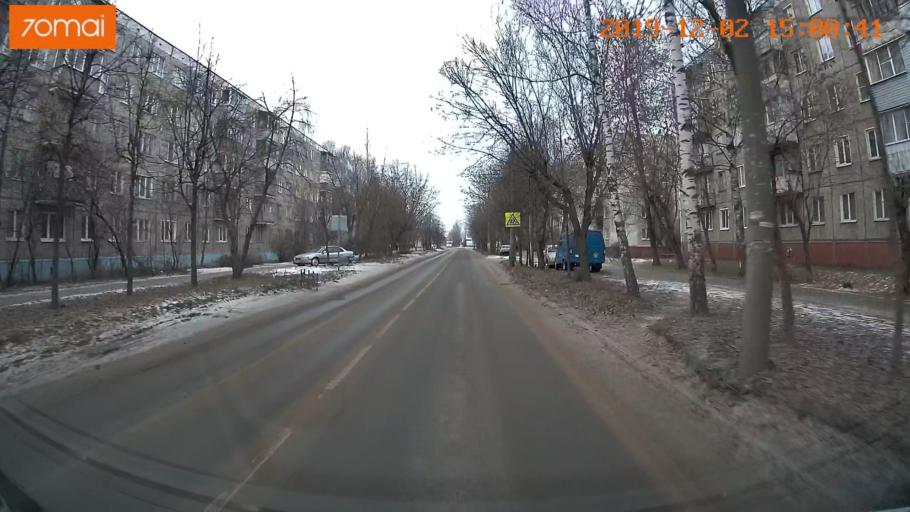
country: RU
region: Ivanovo
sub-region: Gorod Ivanovo
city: Ivanovo
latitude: 56.9717
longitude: 41.0025
